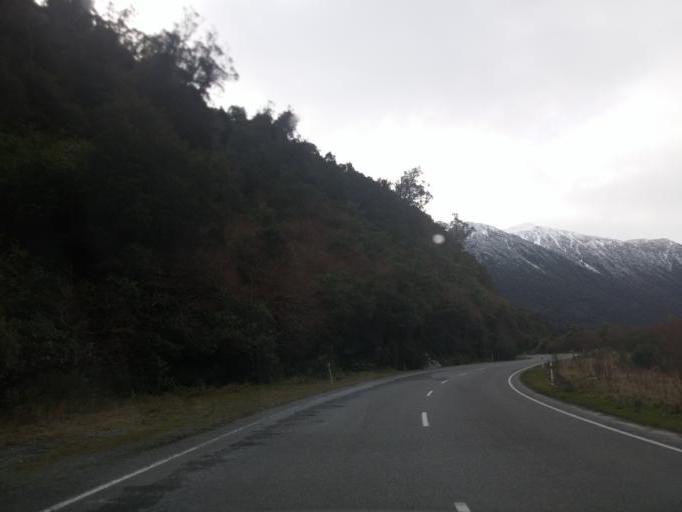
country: NZ
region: West Coast
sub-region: Grey District
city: Greymouth
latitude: -42.8209
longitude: 171.5628
